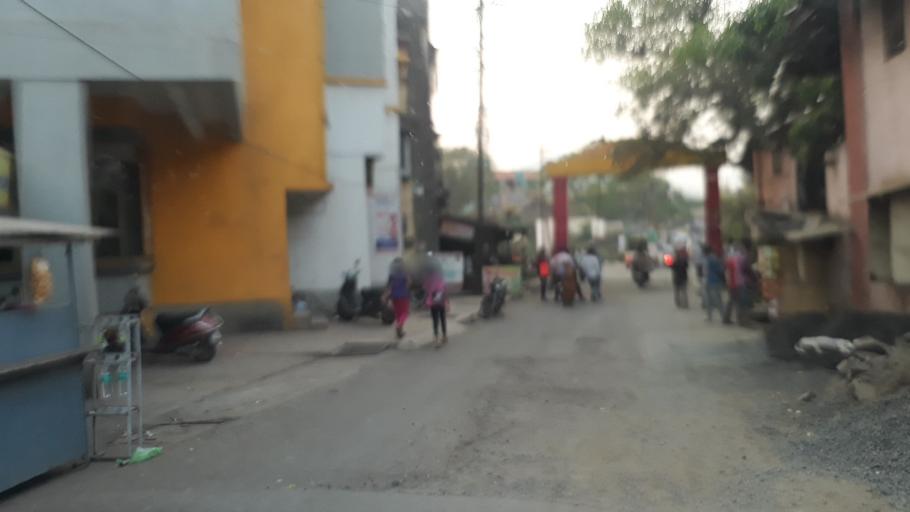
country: IN
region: Maharashtra
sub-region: Raigarh
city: Neral
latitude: 19.0226
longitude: 73.3182
